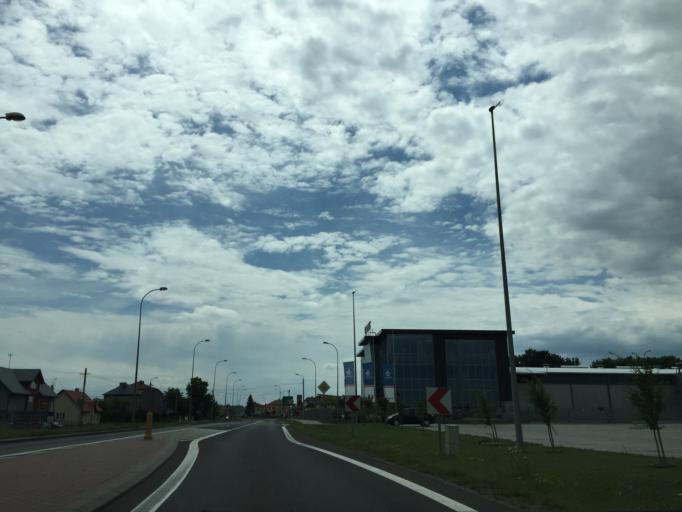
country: PL
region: Podlasie
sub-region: Powiat bielski
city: Bielsk Podlaski
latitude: 52.7846
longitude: 23.1875
